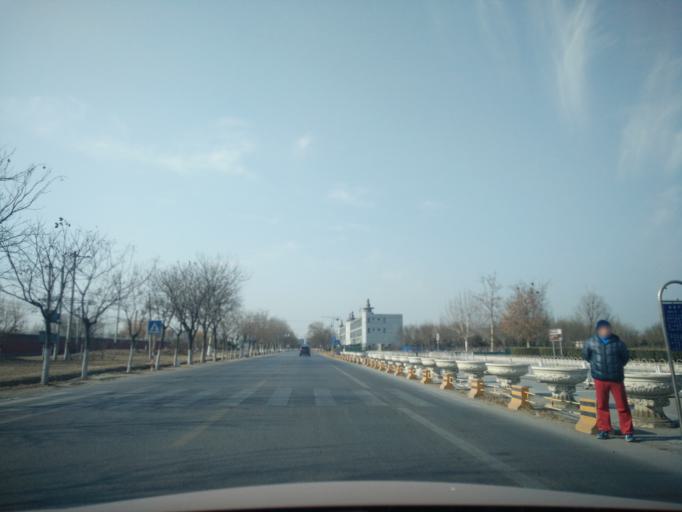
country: CN
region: Beijing
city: Yinghai
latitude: 39.7650
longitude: 116.4666
